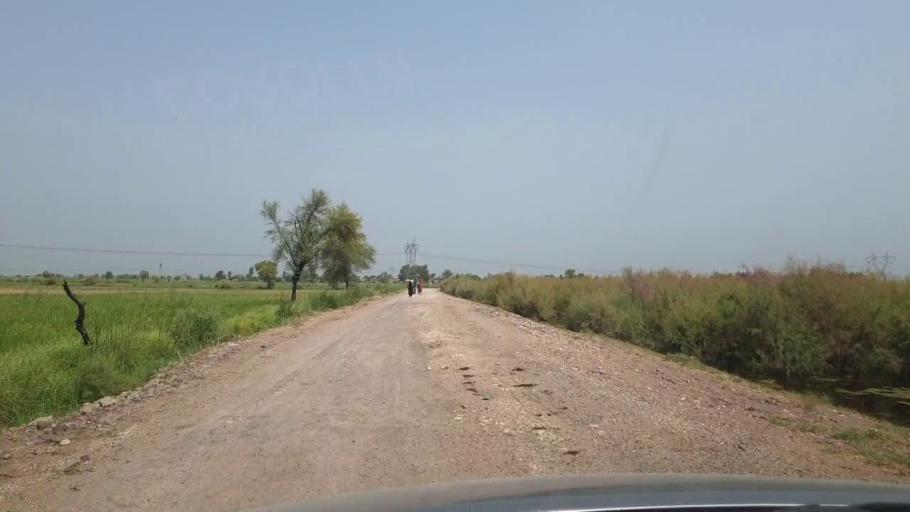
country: PK
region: Sindh
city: Madeji
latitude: 27.8018
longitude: 68.5207
